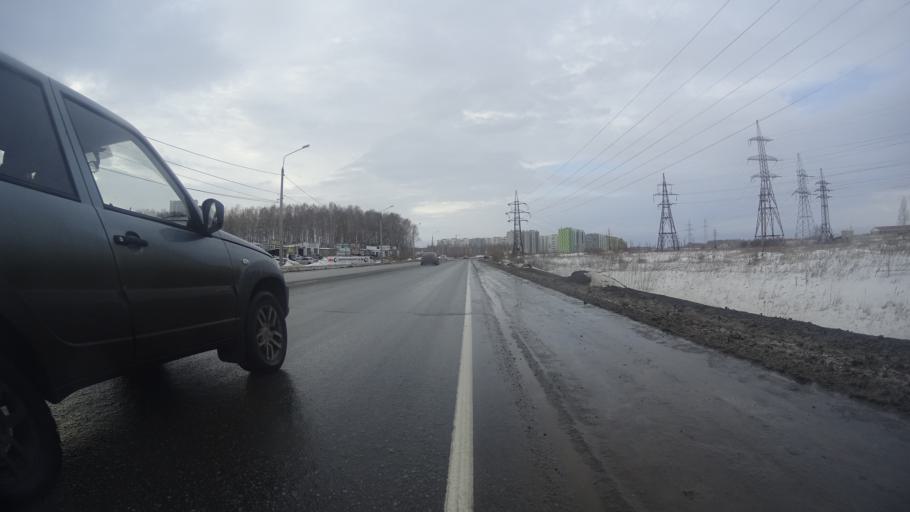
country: RU
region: Chelyabinsk
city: Roshchino
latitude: 55.2105
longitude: 61.3120
